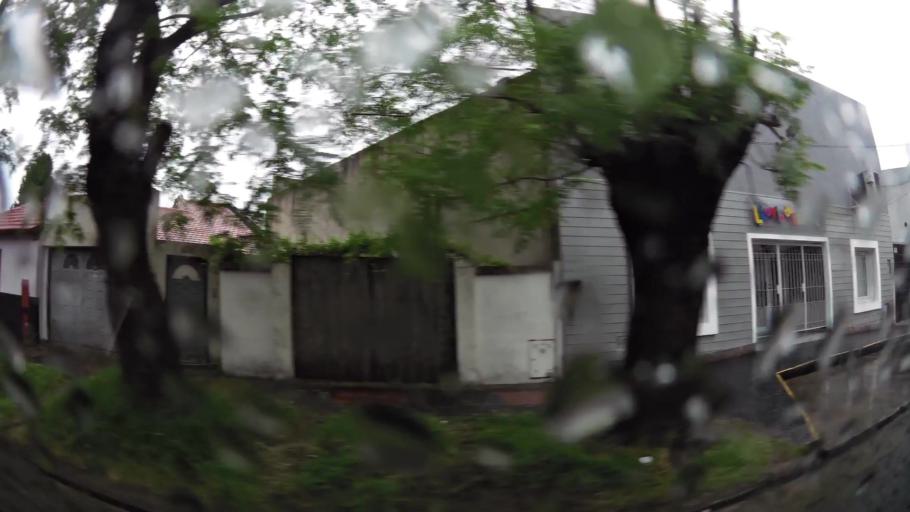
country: AR
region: Buenos Aires
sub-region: Partido de Lanus
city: Lanus
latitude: -34.7041
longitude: -58.4032
